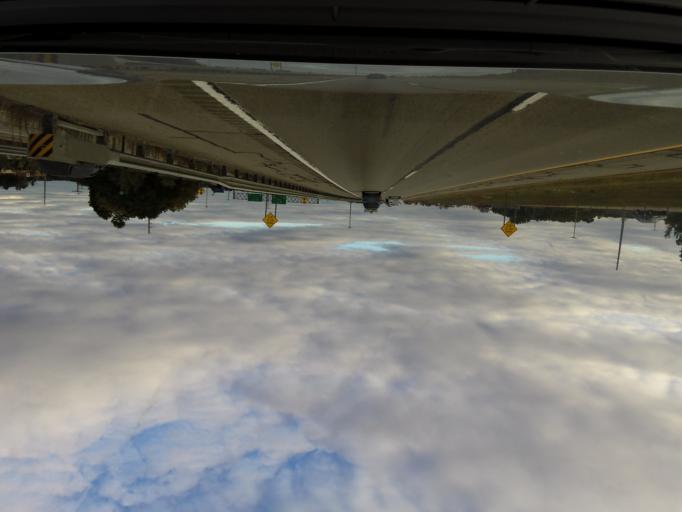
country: US
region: Michigan
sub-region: Livingston County
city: Brighton
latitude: 42.6306
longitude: -83.7486
